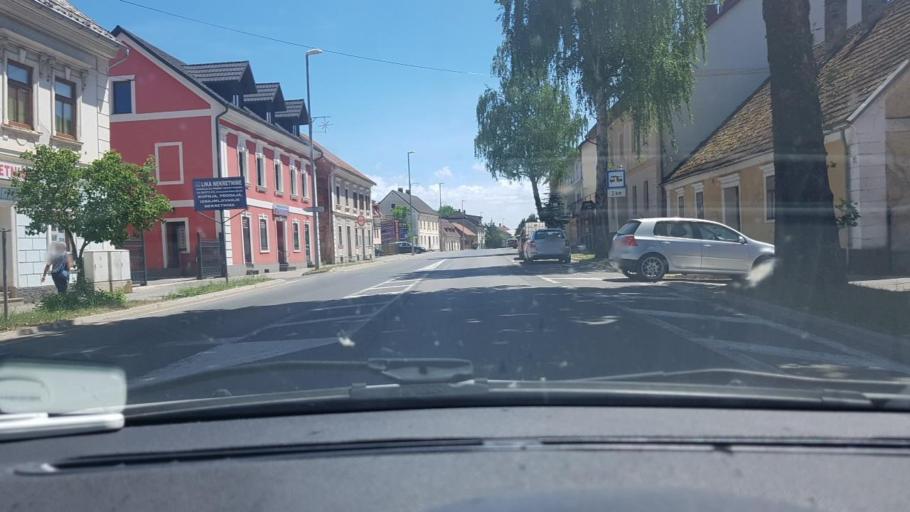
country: HR
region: Licko-Senjska
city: Otocac
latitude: 44.8695
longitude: 15.2411
